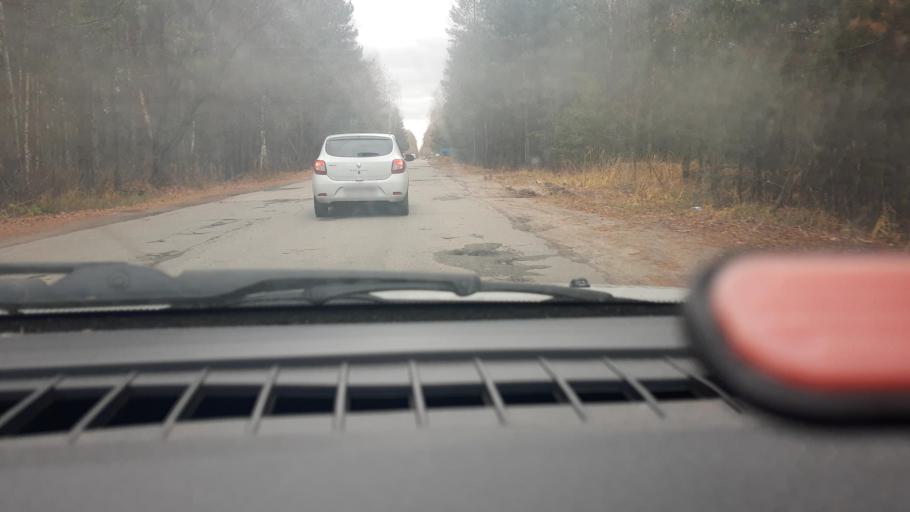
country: RU
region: Nizjnij Novgorod
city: Babino
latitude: 56.3042
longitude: 43.6621
